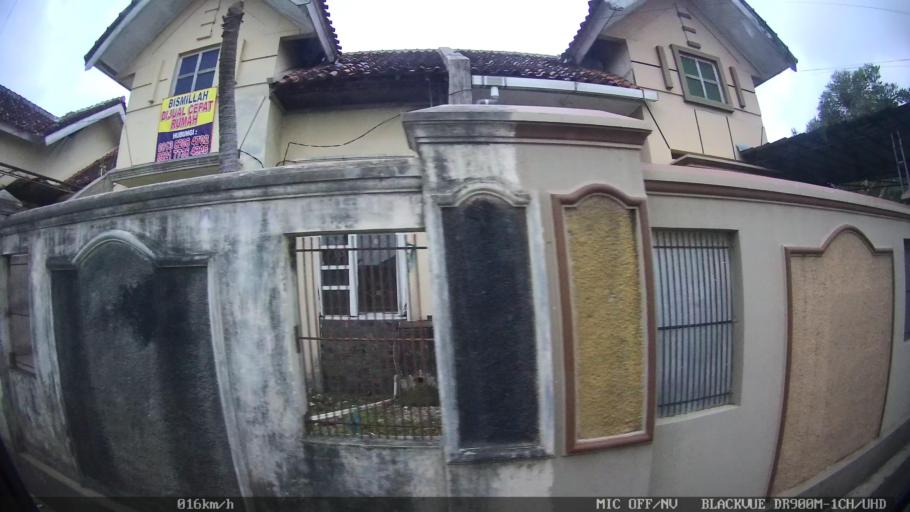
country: ID
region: Lampung
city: Bandarlampung
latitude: -5.4100
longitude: 105.2751
